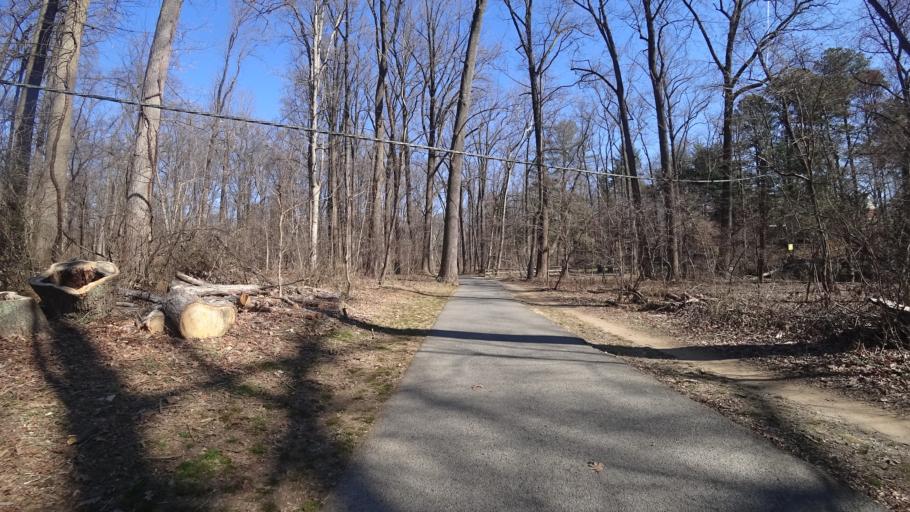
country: US
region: Maryland
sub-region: Montgomery County
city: Kemp Mill
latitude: 39.0325
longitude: -77.0300
